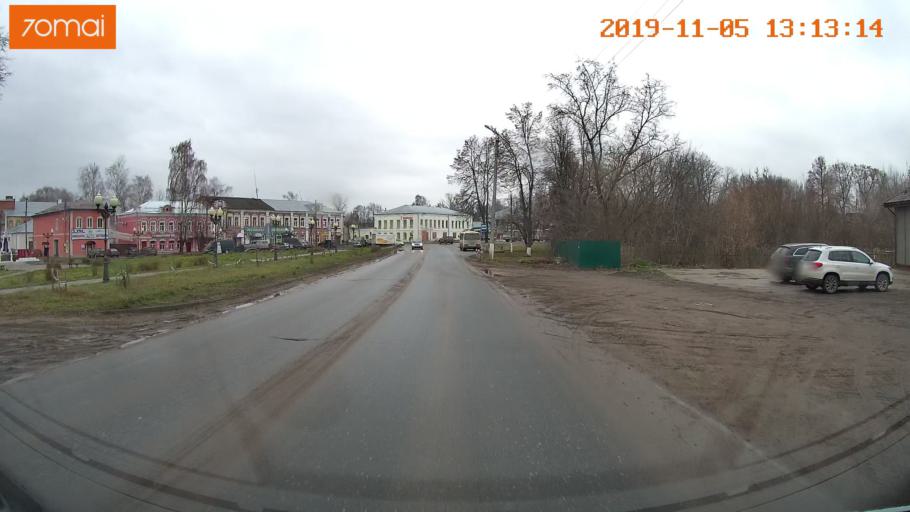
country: RU
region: Ivanovo
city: Shuya
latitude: 56.8522
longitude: 41.3534
